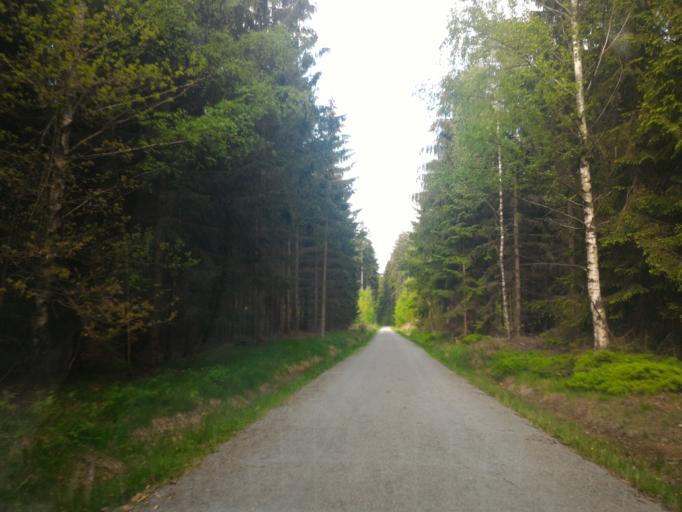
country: DE
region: Saxony
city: Neugersdorf
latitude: 50.9579
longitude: 14.6122
